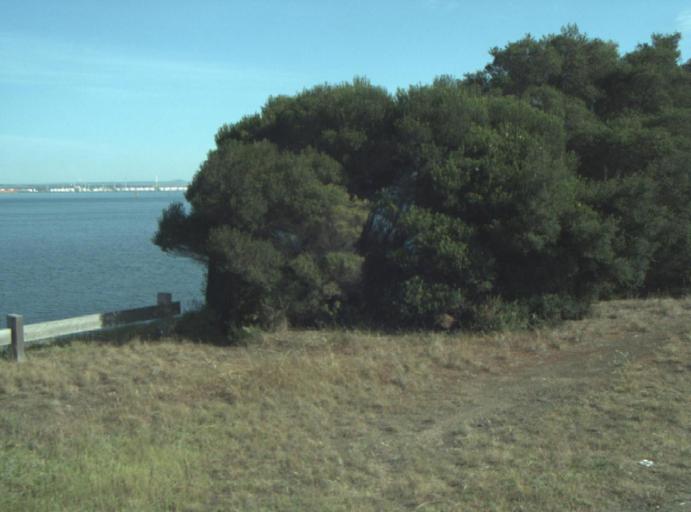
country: AU
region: Victoria
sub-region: Greater Geelong
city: East Geelong
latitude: -38.1333
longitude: 144.4210
